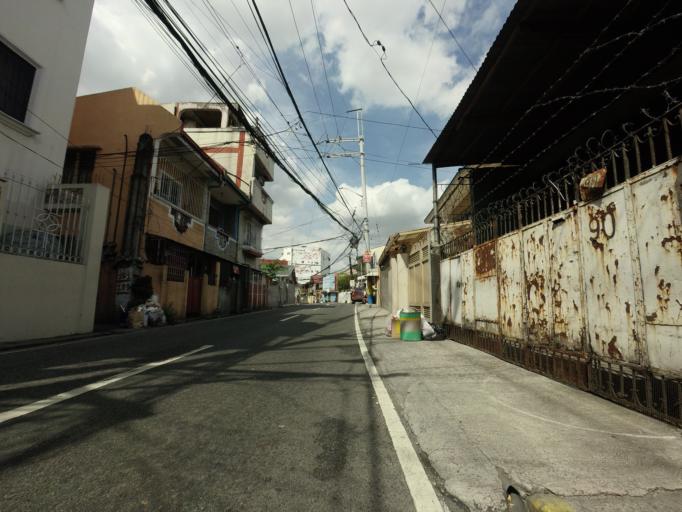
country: PH
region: Metro Manila
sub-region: Mandaluyong
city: Mandaluyong City
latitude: 14.5885
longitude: 121.0319
